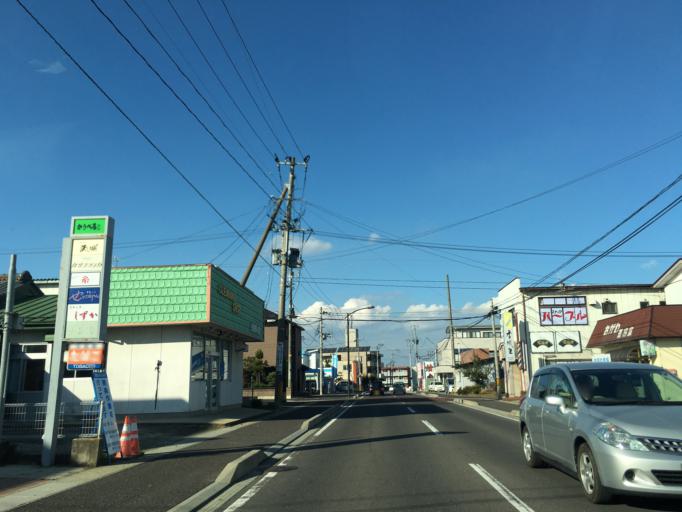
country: JP
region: Fukushima
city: Koriyama
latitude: 37.3996
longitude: 140.3341
